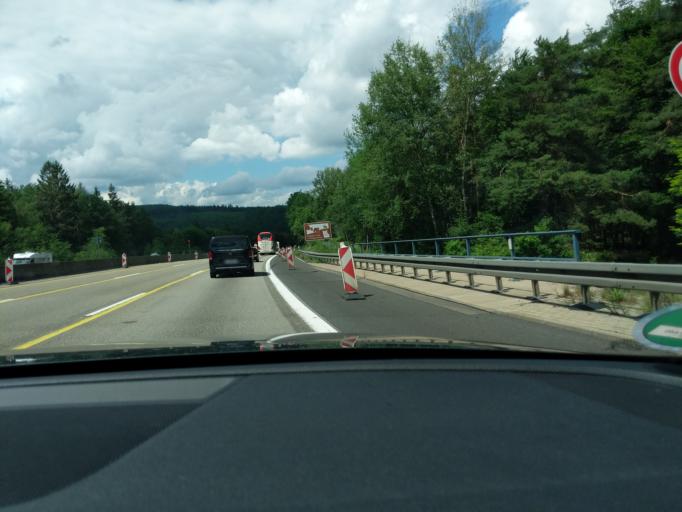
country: DE
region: Hesse
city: Schwarzenborn
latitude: 50.9590
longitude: 9.4915
